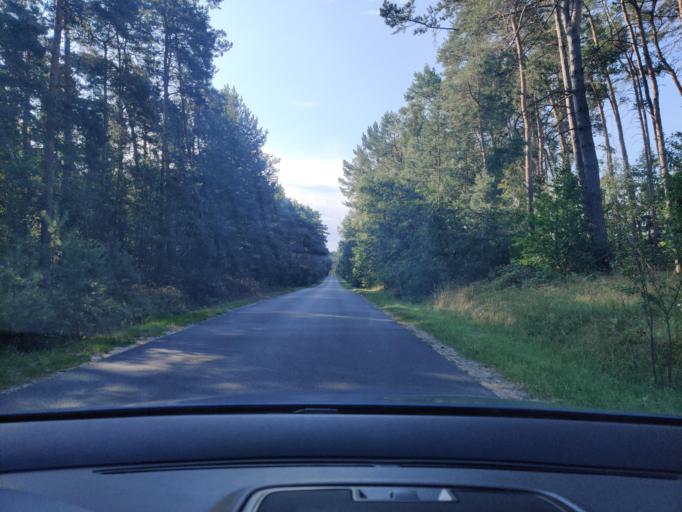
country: PL
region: Greater Poland Voivodeship
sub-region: Konin
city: Konin
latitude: 52.1807
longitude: 18.3340
